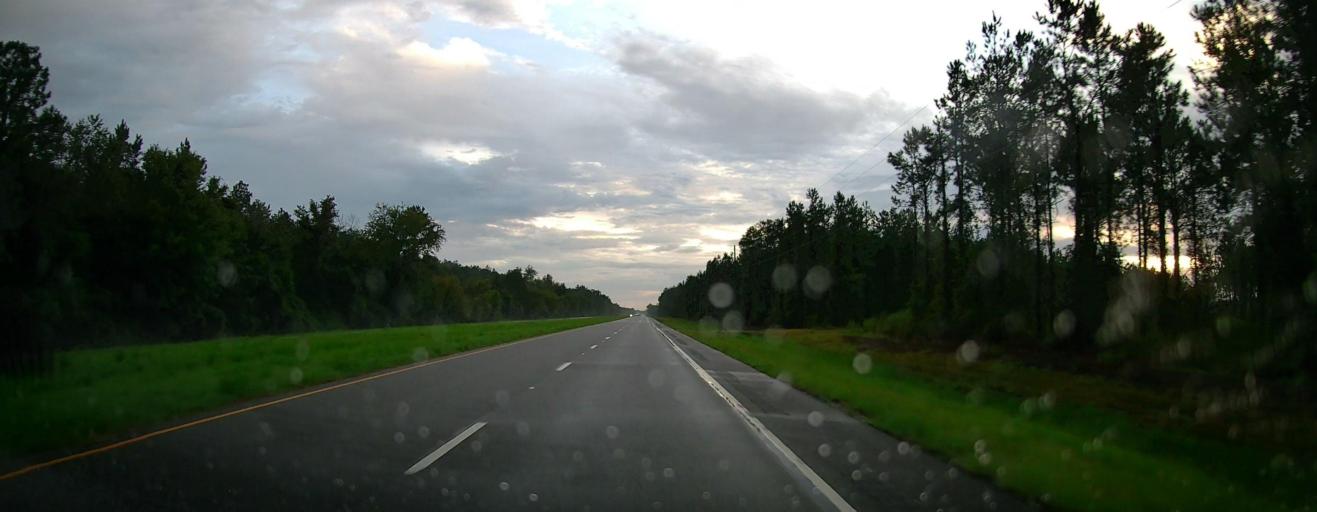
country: US
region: Georgia
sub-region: Lanier County
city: Lakeland
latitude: 30.9584
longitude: -82.9497
